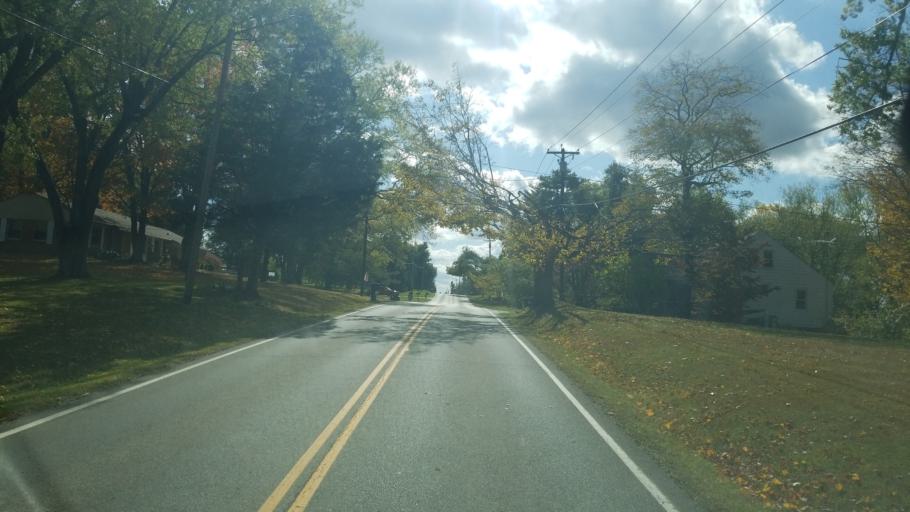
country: US
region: Ohio
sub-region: Warren County
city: South Lebanon
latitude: 39.3937
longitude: -84.1709
